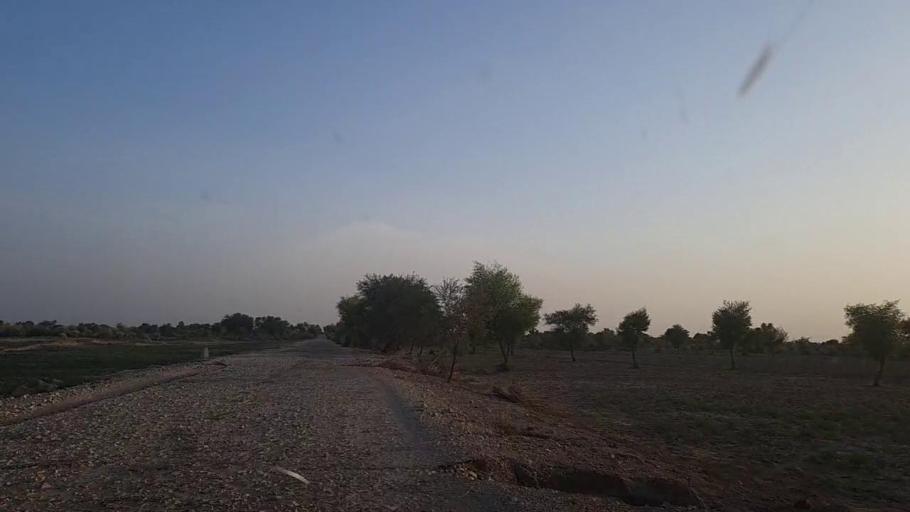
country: PK
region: Sindh
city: Khanpur
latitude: 27.6078
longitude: 69.4356
